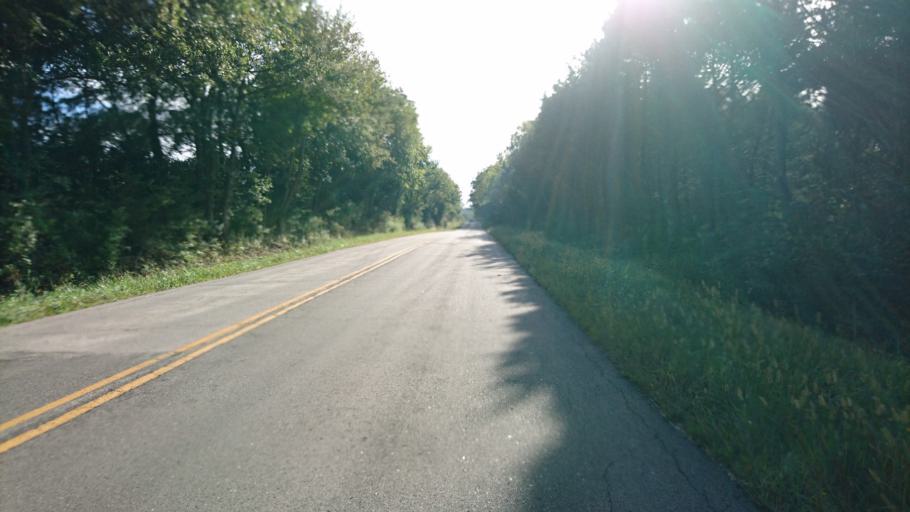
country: US
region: Missouri
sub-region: Crawford County
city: Cuba
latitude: 38.1041
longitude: -91.3459
